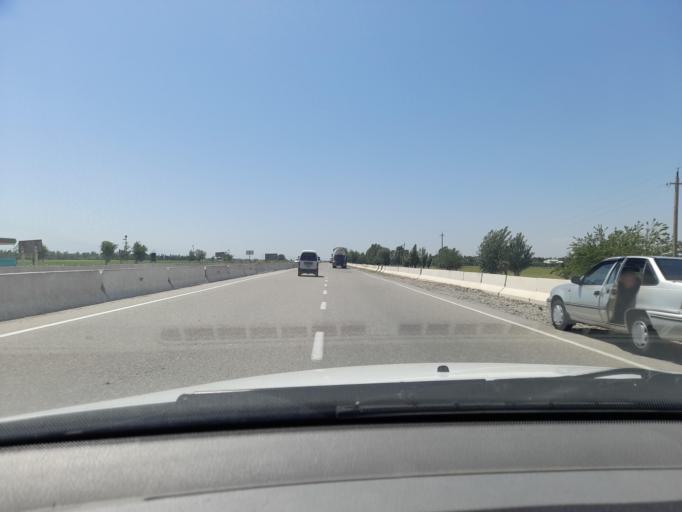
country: UZ
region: Jizzax
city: Dustlik
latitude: 40.3660
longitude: 68.1488
